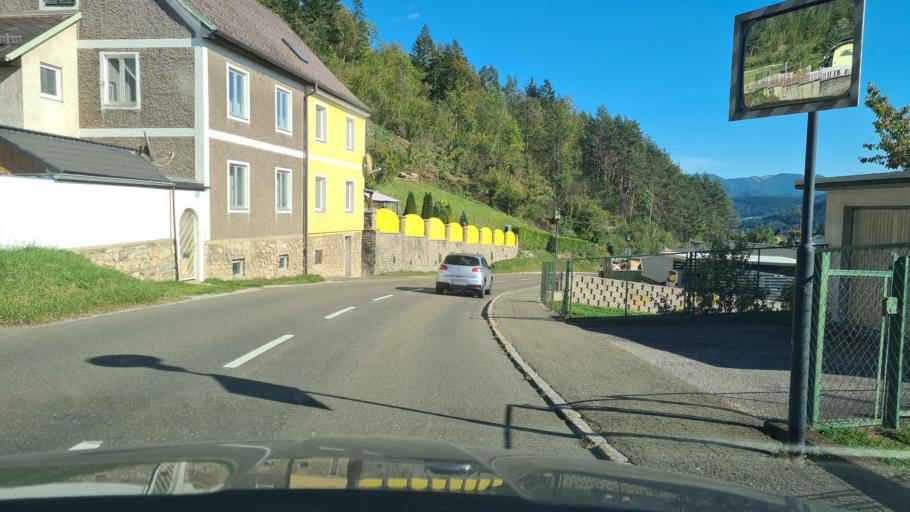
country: AT
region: Styria
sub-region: Politischer Bezirk Leoben
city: Sankt Peter-Freienstein
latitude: 47.4019
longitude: 15.0212
